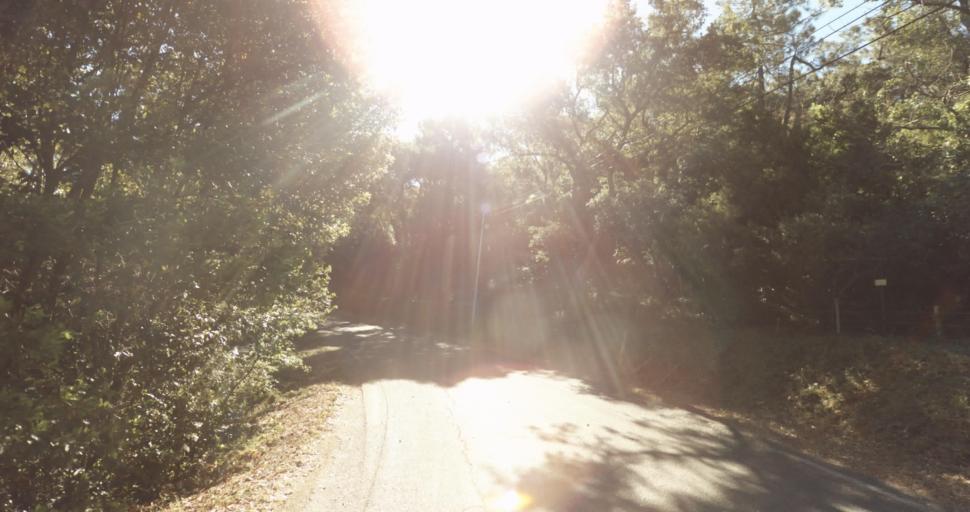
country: FR
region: Provence-Alpes-Cote d'Azur
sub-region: Departement du Var
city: Gassin
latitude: 43.2221
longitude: 6.5902
